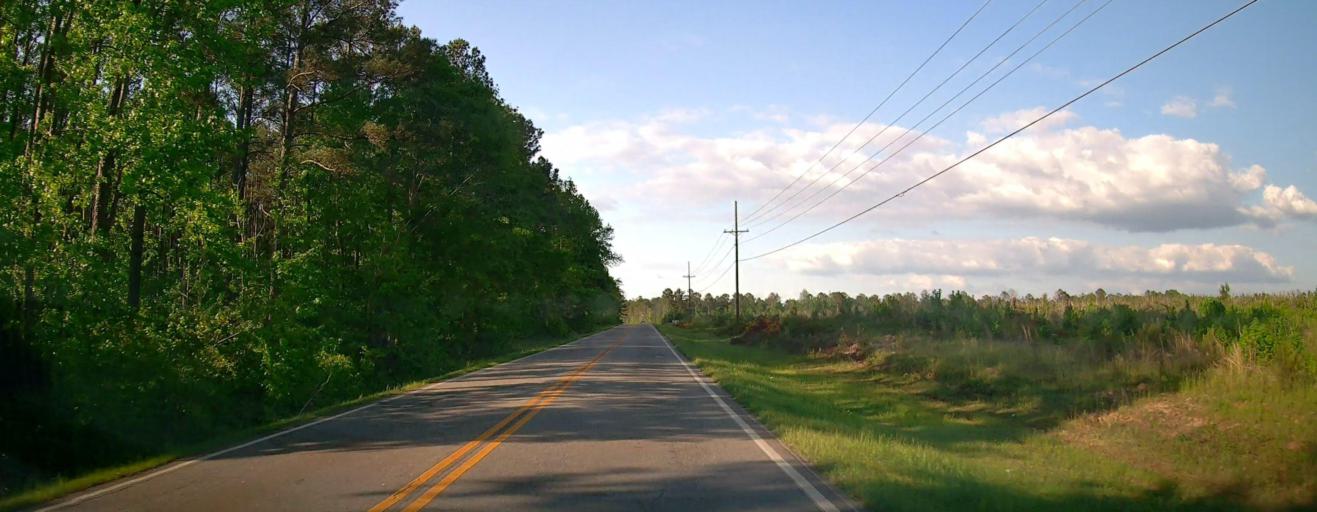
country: US
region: Georgia
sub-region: Putnam County
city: Eatonton
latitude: 33.2524
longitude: -83.3029
